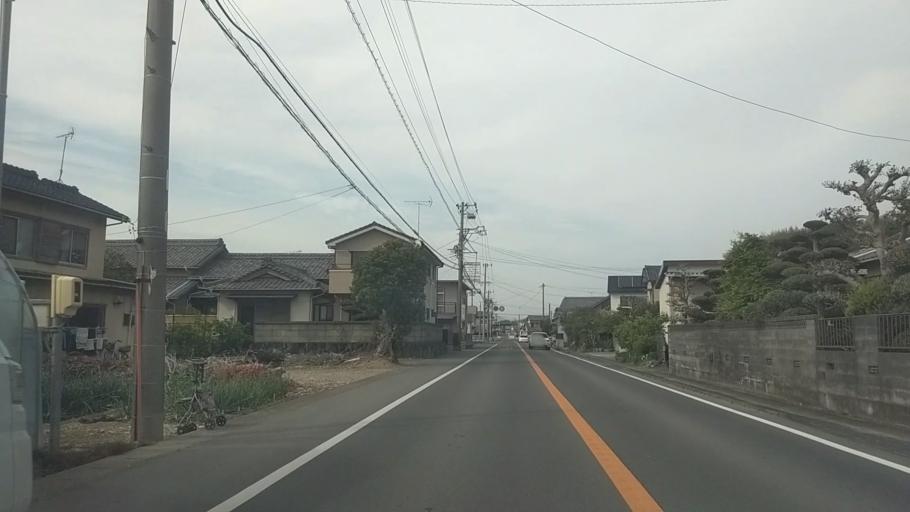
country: JP
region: Shizuoka
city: Kosai-shi
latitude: 34.7260
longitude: 137.6315
